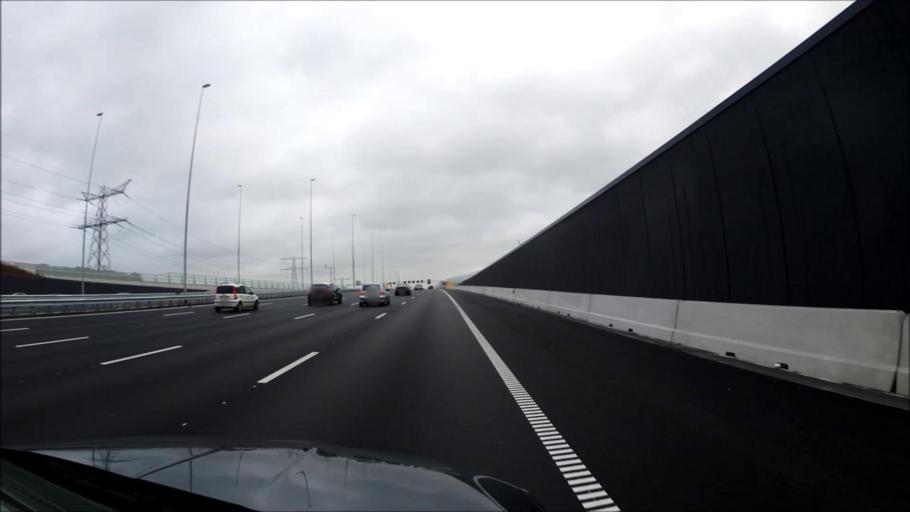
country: NL
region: North Holland
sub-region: Gemeente Weesp
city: Weesp
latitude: 52.3231
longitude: 5.0655
